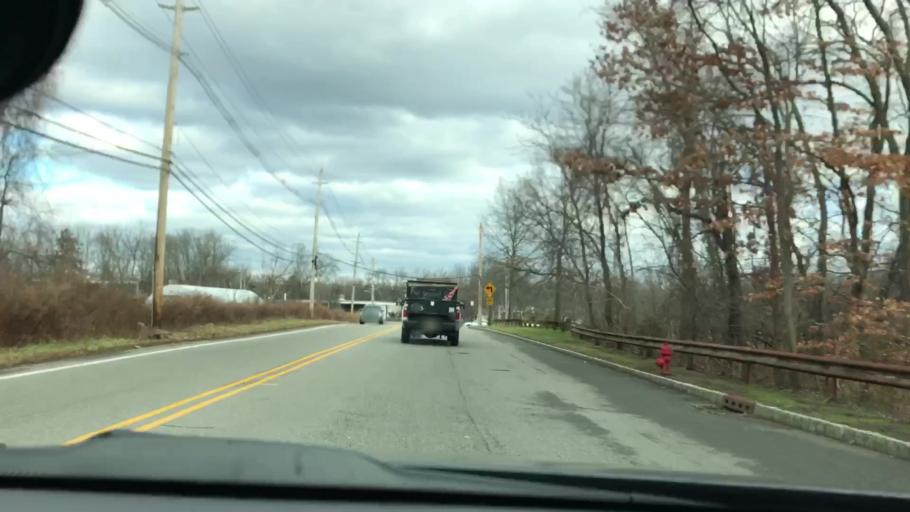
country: US
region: New Jersey
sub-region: Morris County
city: East Hanover
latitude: 40.8377
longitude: -74.3414
